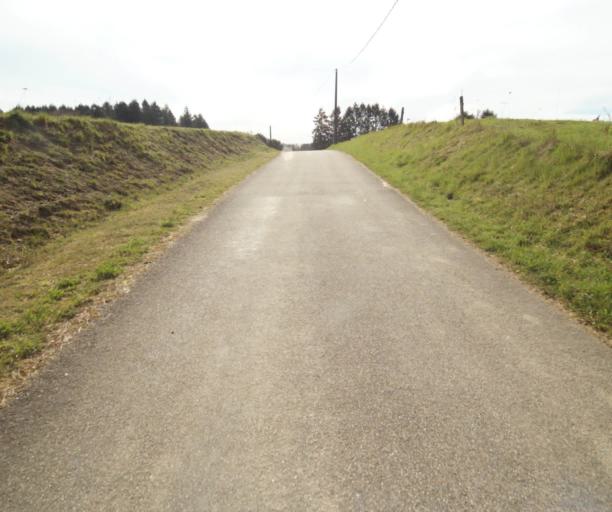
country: FR
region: Limousin
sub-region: Departement de la Correze
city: Correze
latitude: 45.3519
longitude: 1.8687
